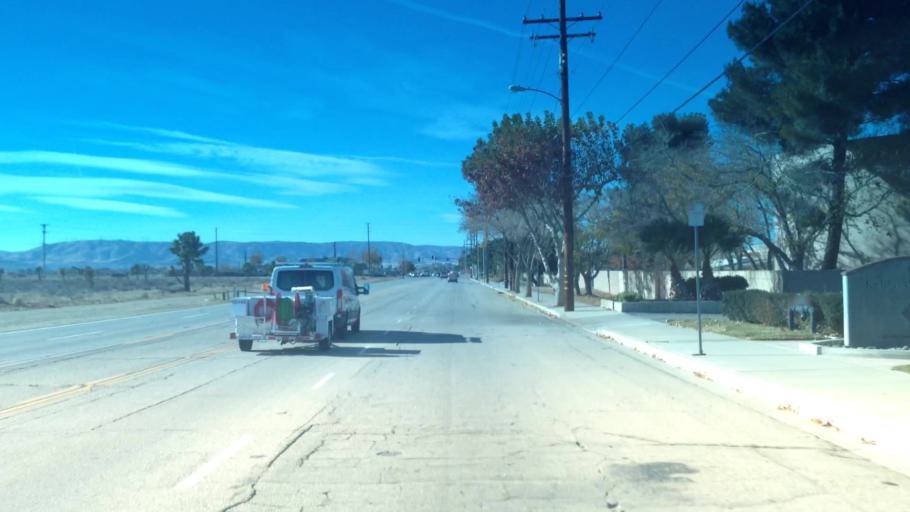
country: US
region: California
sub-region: Los Angeles County
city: Lancaster
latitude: 34.6459
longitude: -118.1439
